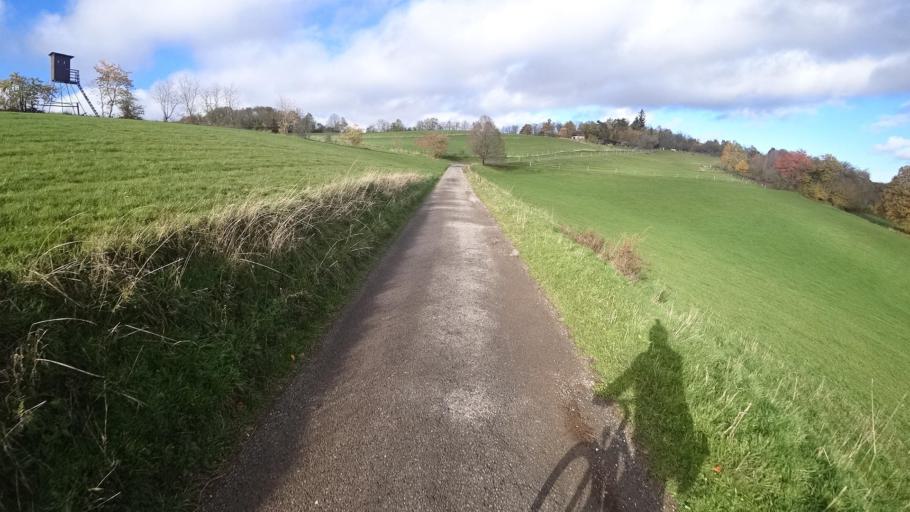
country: DE
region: Rheinland-Pfalz
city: Lind
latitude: 50.4885
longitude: 6.9383
